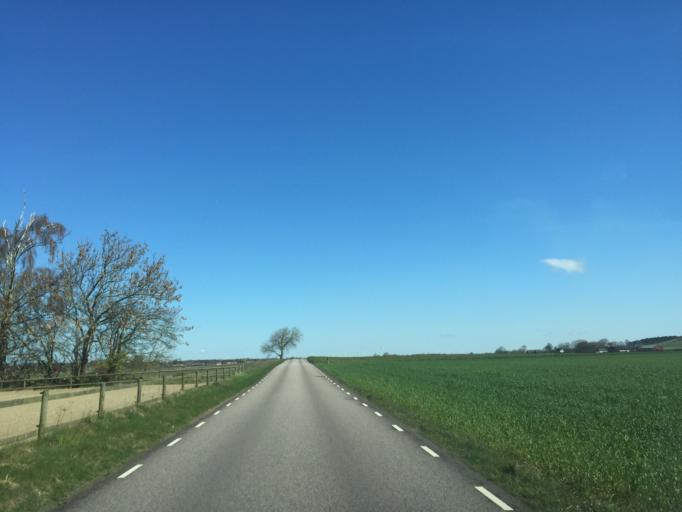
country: SE
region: Skane
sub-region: Kavlinge Kommun
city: Loddekopinge
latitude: 55.8008
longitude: 13.0249
